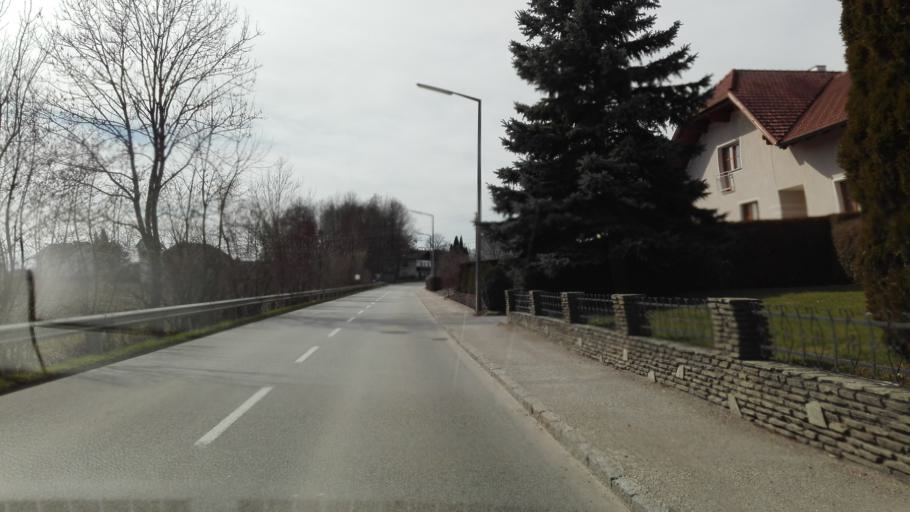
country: AT
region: Upper Austria
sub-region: Politischer Bezirk Scharding
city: Sankt Marienkirchen bei Schaerding
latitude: 48.3713
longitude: 13.5510
